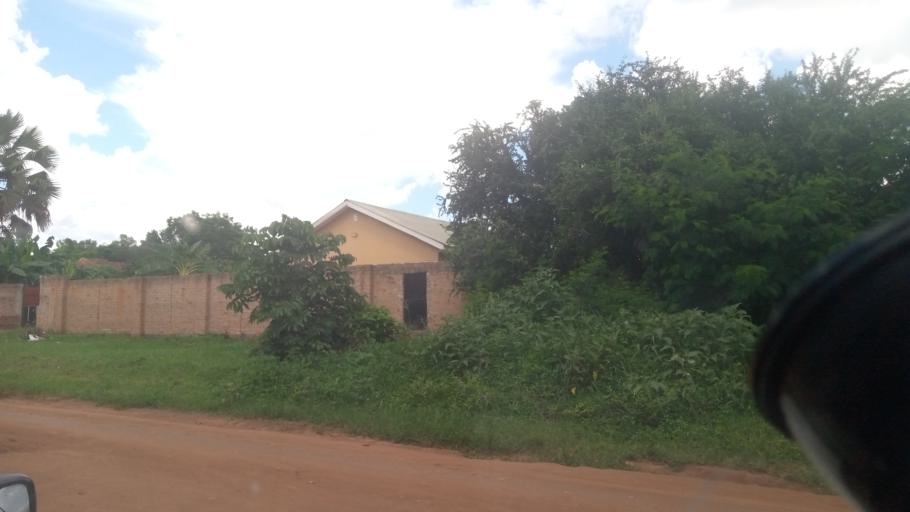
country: UG
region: Northern Region
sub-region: Lira District
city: Lira
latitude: 2.2389
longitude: 32.9025
